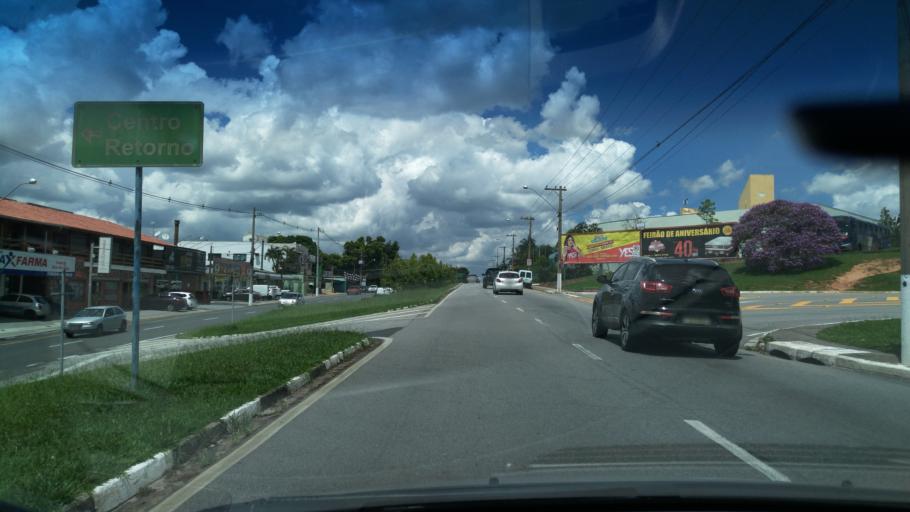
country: BR
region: Sao Paulo
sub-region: Vinhedo
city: Vinhedo
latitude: -23.0274
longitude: -46.9816
